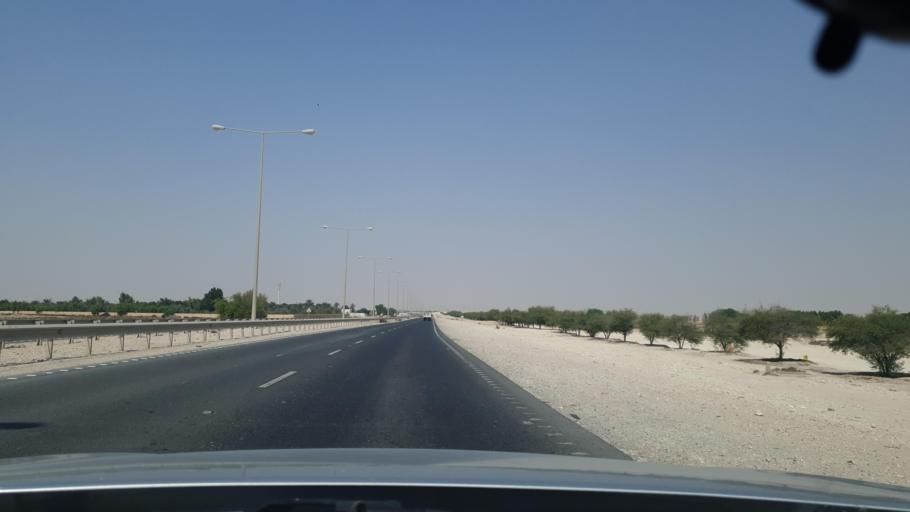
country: QA
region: Al Khawr
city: Al Khawr
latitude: 25.7250
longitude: 51.4973
